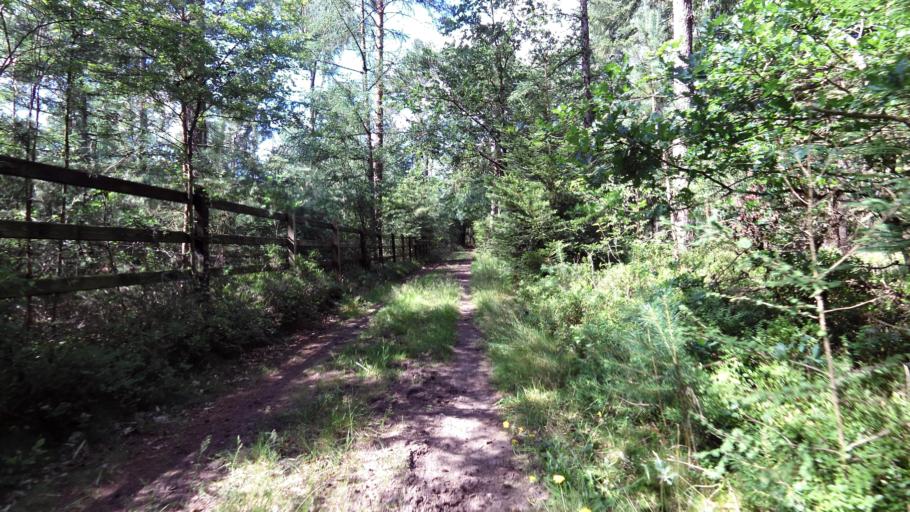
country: NL
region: Gelderland
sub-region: Gemeente Epe
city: Vaassen
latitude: 52.2672
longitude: 5.9279
